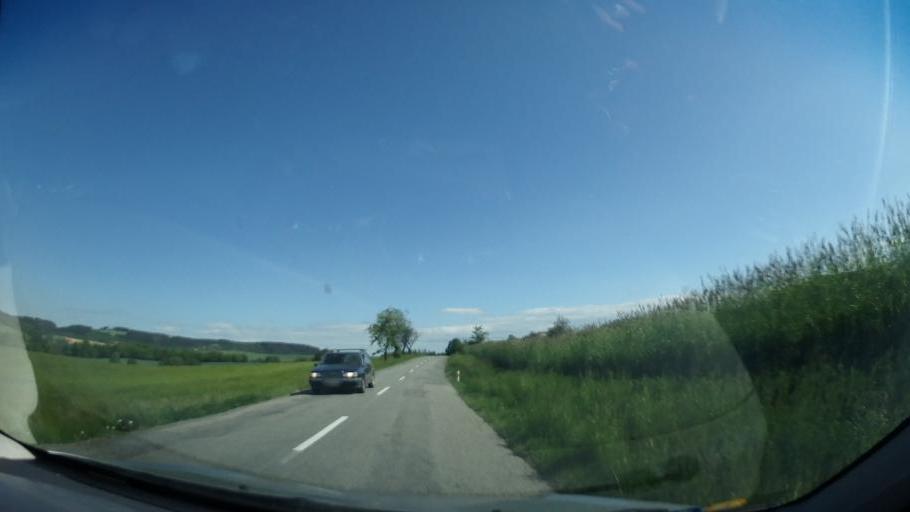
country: CZ
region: South Moravian
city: Velke Opatovice
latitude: 49.6113
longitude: 16.6078
